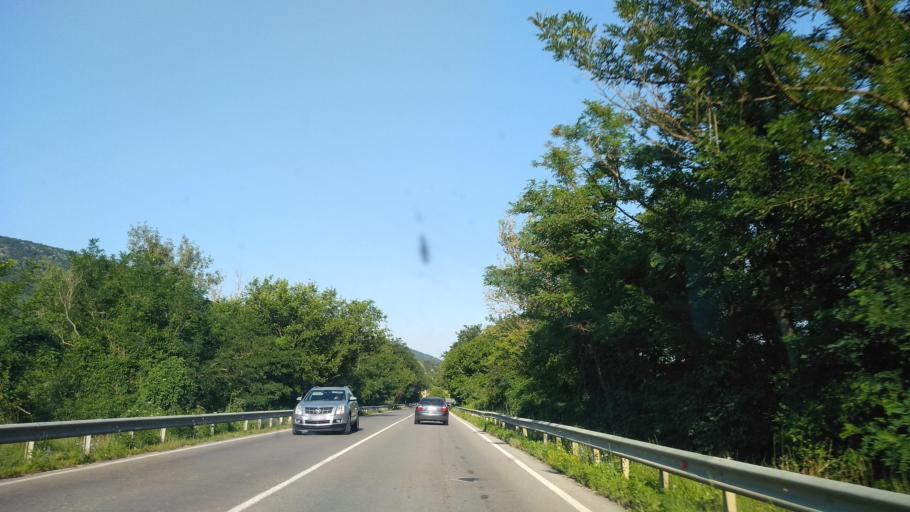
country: BG
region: Lovech
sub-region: Obshtina Lovech
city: Lovech
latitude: 43.0404
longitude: 24.7127
